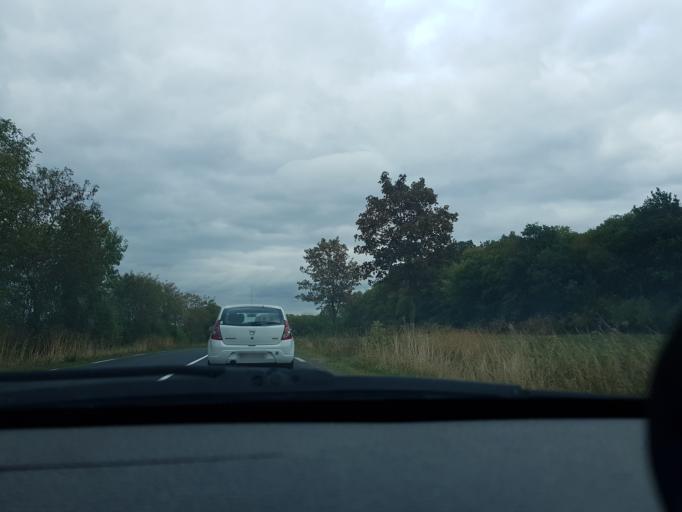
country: FR
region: Lorraine
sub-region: Departement de la Moselle
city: Chateau-Salins
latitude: 48.7691
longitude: 6.4421
